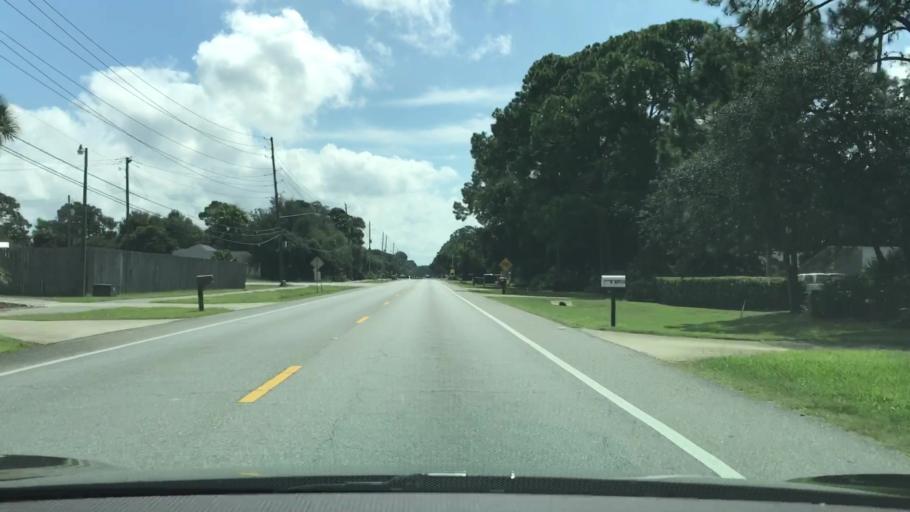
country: US
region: Florida
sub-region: Bay County
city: Panama City Beach
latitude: 30.1689
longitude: -85.7833
